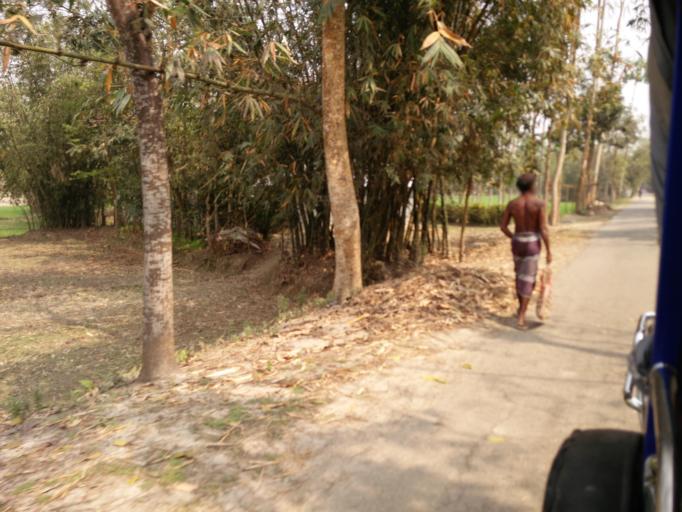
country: BD
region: Rangpur Division
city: Nageswari
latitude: 25.8797
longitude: 89.6828
